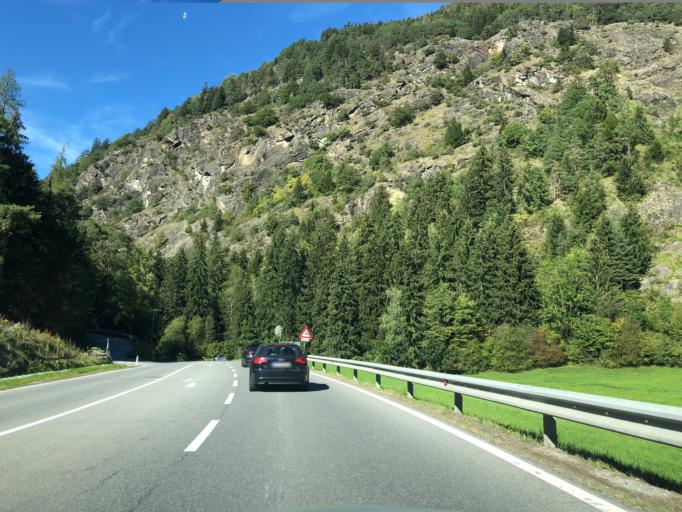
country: AT
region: Tyrol
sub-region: Politischer Bezirk Imst
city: Sautens
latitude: 47.2169
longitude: 10.8669
